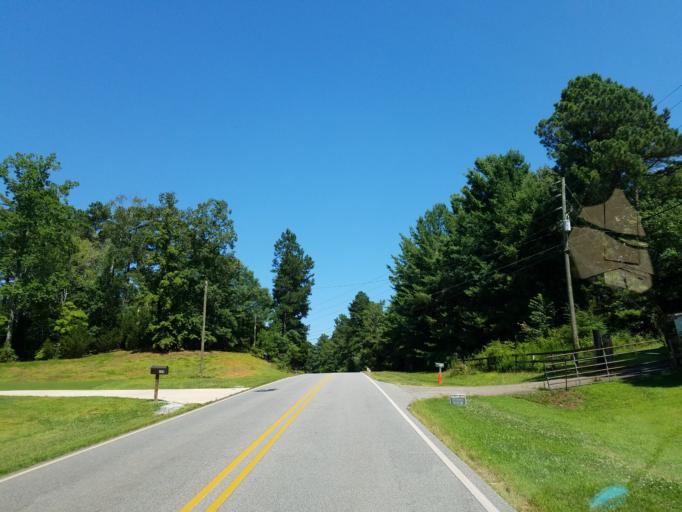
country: US
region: Georgia
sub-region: Dawson County
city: Dawsonville
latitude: 34.3397
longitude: -84.0278
